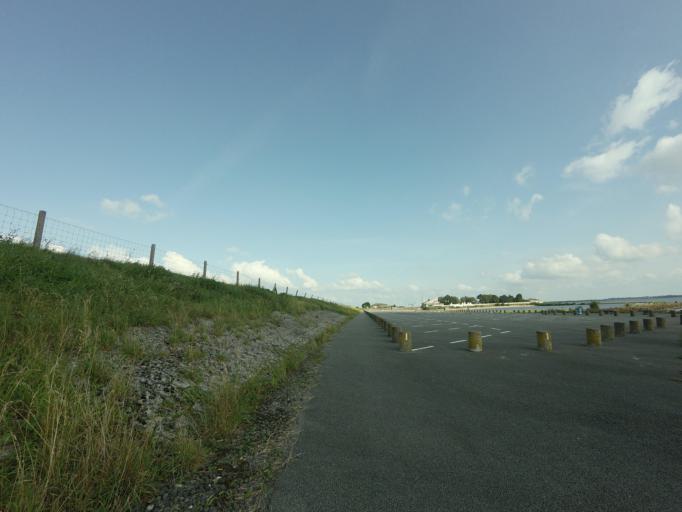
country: NL
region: Flevoland
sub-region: Gemeente Dronten
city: Dronten
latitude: 52.6130
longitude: 5.7401
